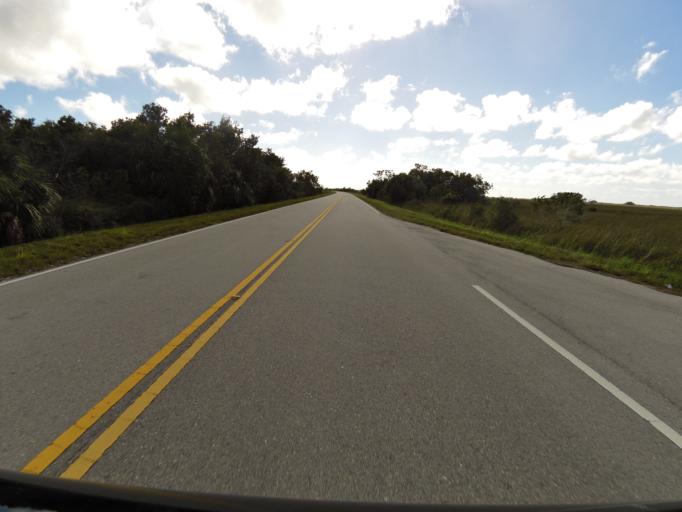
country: US
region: Florida
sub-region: Miami-Dade County
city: Florida City
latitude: 25.3641
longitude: -80.8197
